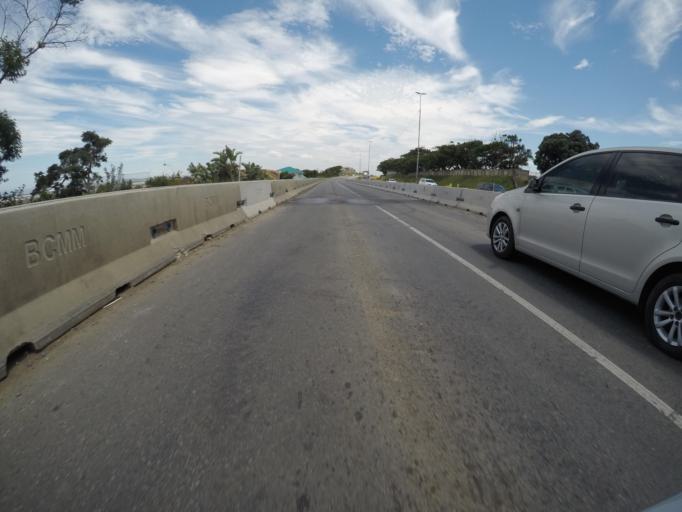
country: ZA
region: Eastern Cape
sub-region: Buffalo City Metropolitan Municipality
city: East London
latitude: -33.0363
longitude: 27.8607
